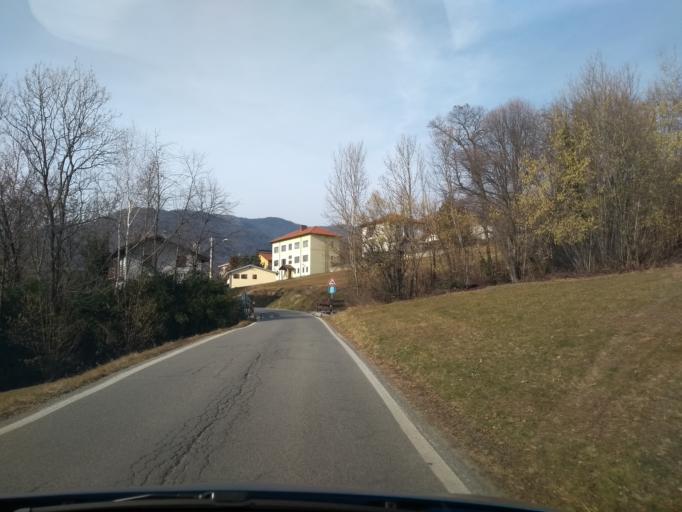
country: IT
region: Piedmont
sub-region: Provincia di Torino
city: Coassolo
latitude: 45.3005
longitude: 7.4815
